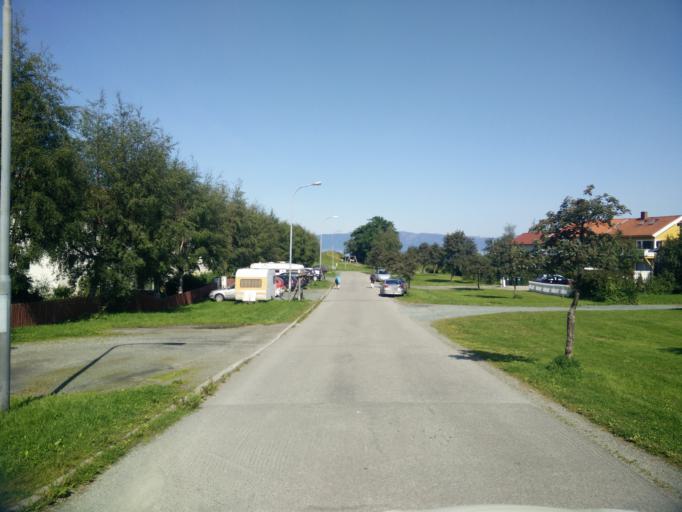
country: NO
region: Sor-Trondelag
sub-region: Trondheim
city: Trondheim
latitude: 63.4482
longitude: 10.4370
